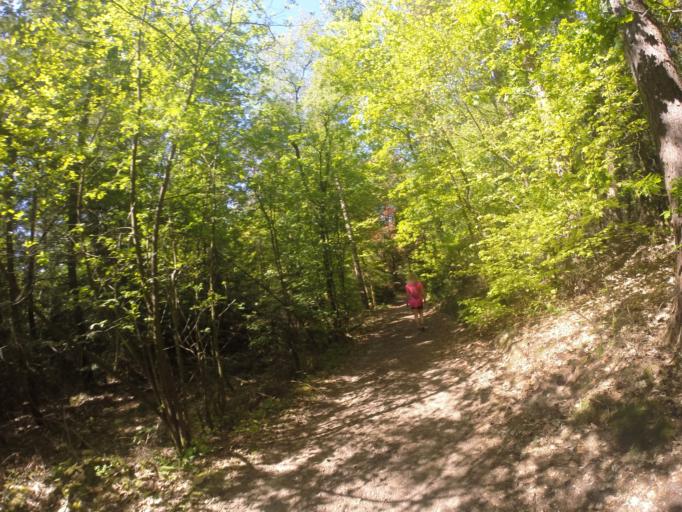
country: NL
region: Gelderland
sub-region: Gemeente Montferland
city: s-Heerenberg
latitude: 51.9198
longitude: 6.2422
